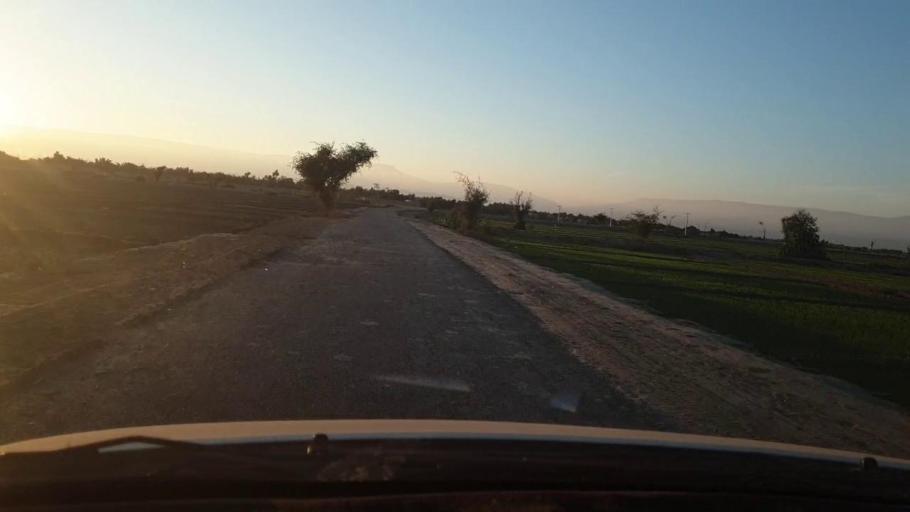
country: PK
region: Sindh
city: Johi
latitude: 26.8293
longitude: 67.4507
